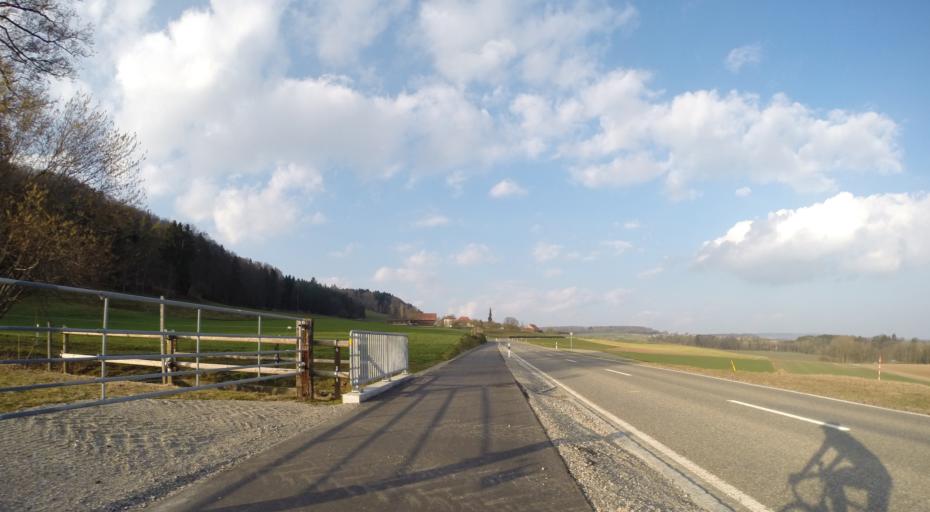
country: CH
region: Thurgau
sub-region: Frauenfeld District
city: Pfyn
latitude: 47.6119
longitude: 8.9163
